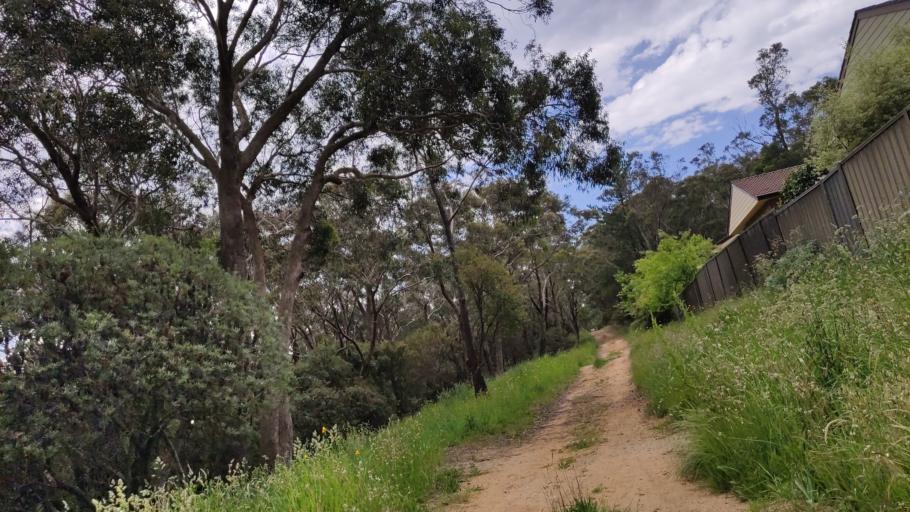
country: AU
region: New South Wales
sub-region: Blue Mountains Municipality
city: Leura
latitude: -33.7176
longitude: 150.3268
